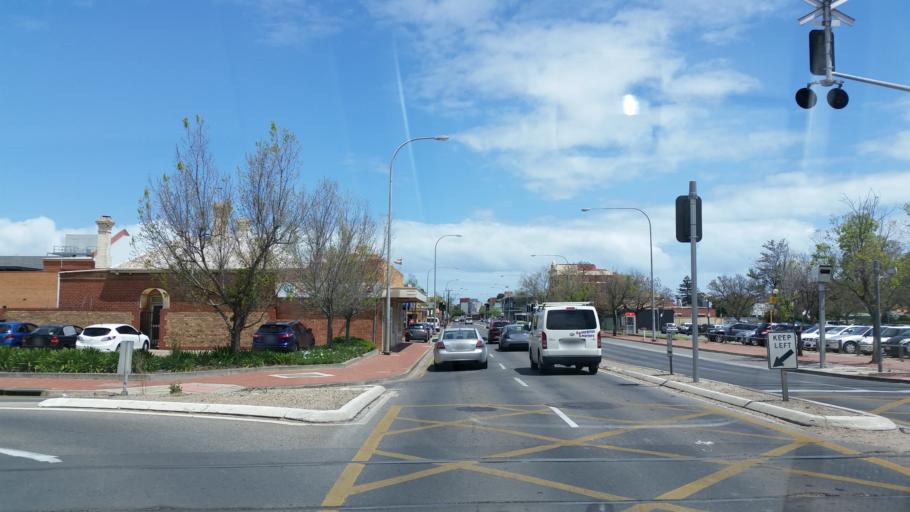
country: AU
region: South Australia
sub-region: Charles Sturt
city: Woodville North
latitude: -34.8775
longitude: 138.5384
